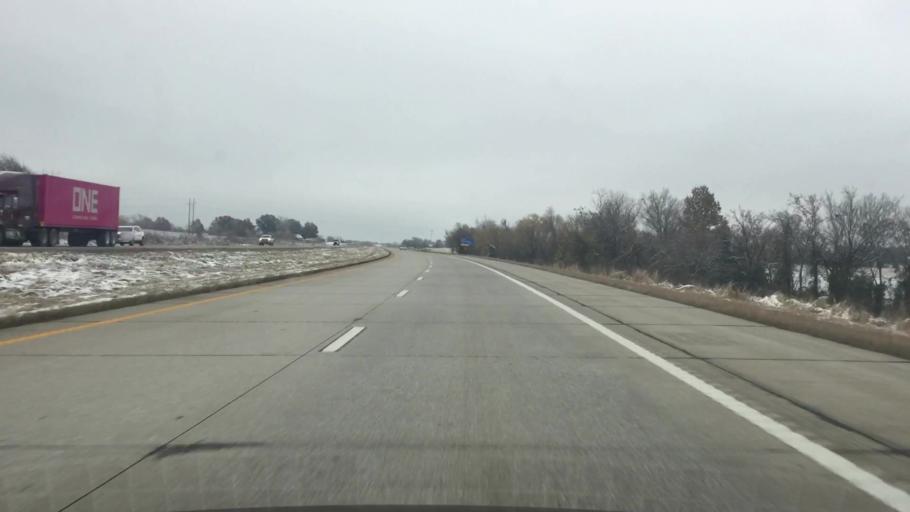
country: US
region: Missouri
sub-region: Saint Clair County
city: Osceola
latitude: 38.1885
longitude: -93.7385
